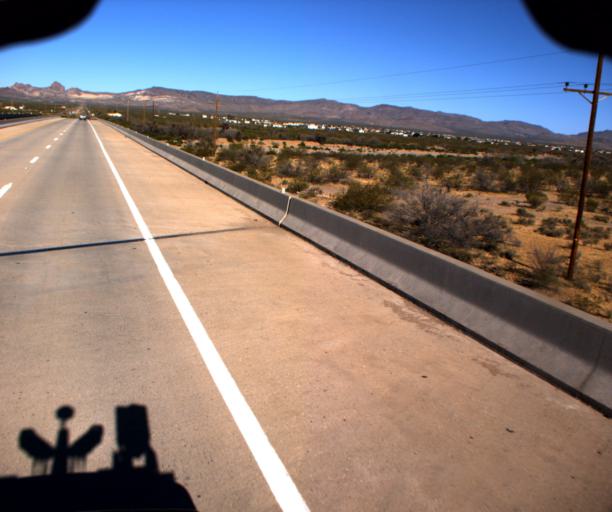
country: US
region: Arizona
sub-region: Mohave County
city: Golden Valley
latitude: 35.2253
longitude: -114.2807
